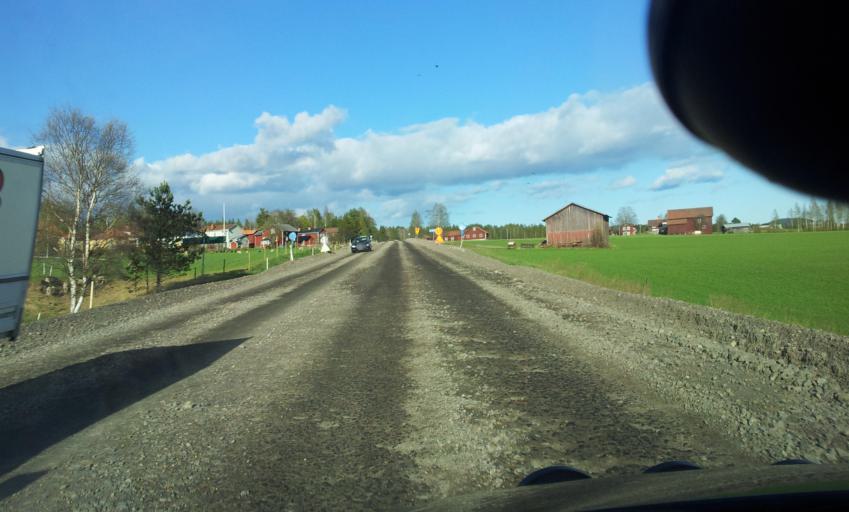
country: SE
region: Gaevleborg
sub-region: Bollnas Kommun
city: Kilafors
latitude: 61.3509
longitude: 16.6884
